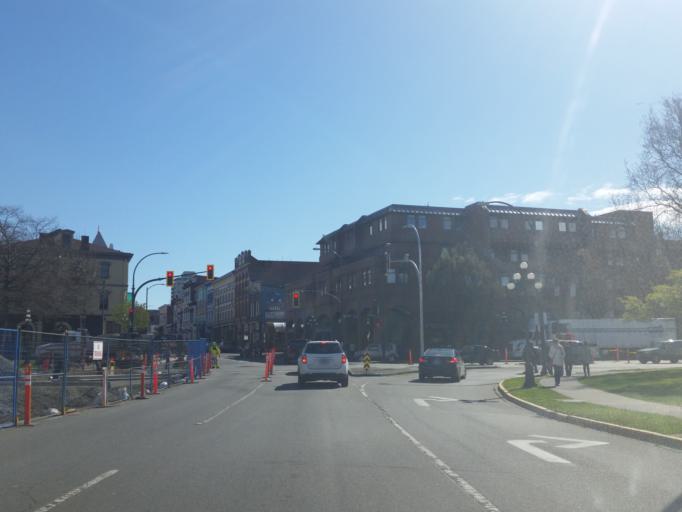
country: CA
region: British Columbia
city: Victoria
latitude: 48.4281
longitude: -123.3707
